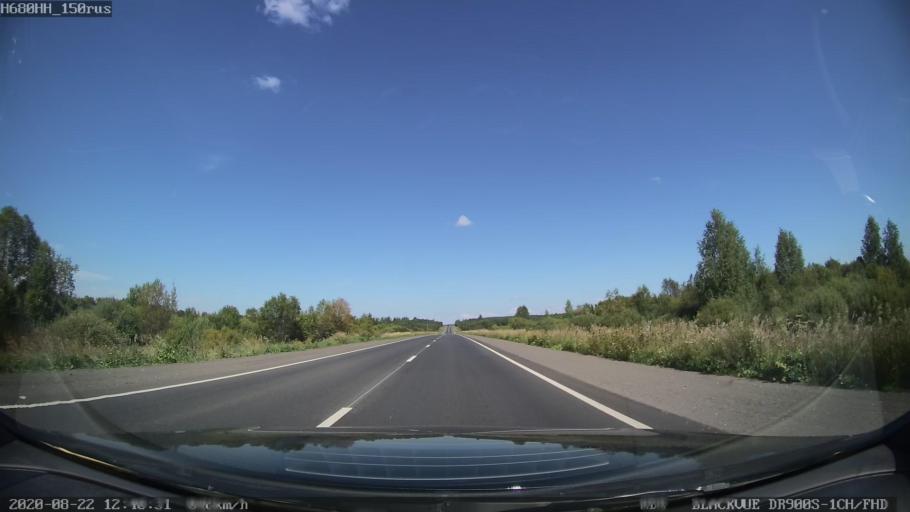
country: RU
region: Tverskaya
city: Rameshki
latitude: 57.3355
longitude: 36.0947
